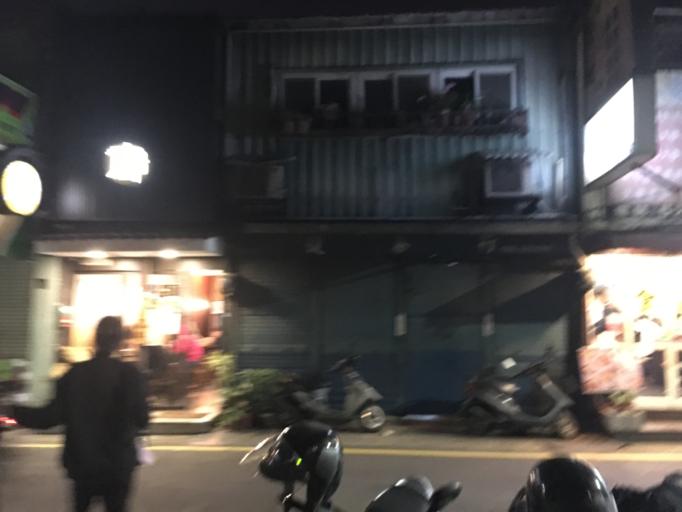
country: TW
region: Taiwan
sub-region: Hsinchu
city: Hsinchu
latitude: 24.8057
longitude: 120.9713
